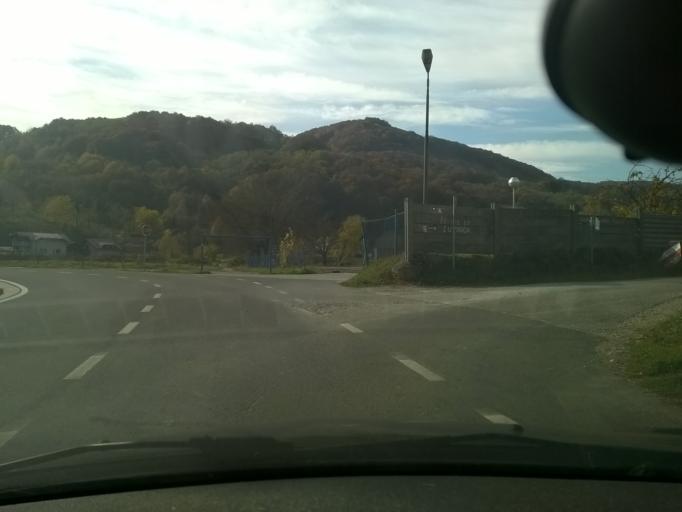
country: HR
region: Krapinsko-Zagorska
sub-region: Grad Krapina
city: Krapina
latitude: 46.1807
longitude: 15.8607
